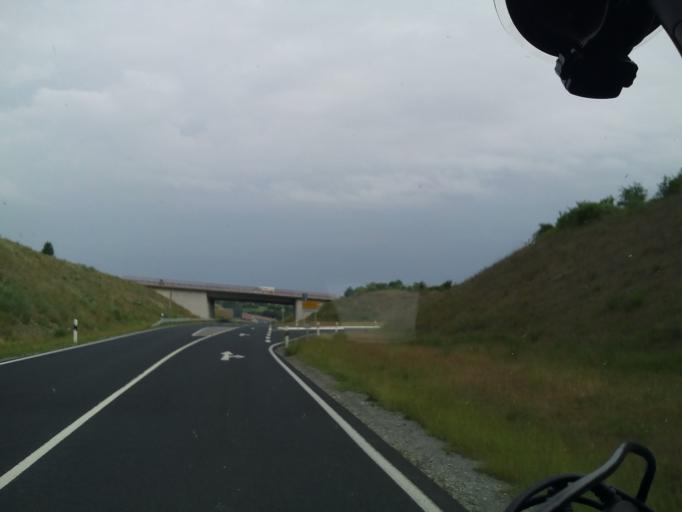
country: DE
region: Bavaria
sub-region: Regierungsbezirk Unterfranken
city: Mellrichstadt
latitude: 50.4465
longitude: 10.3099
